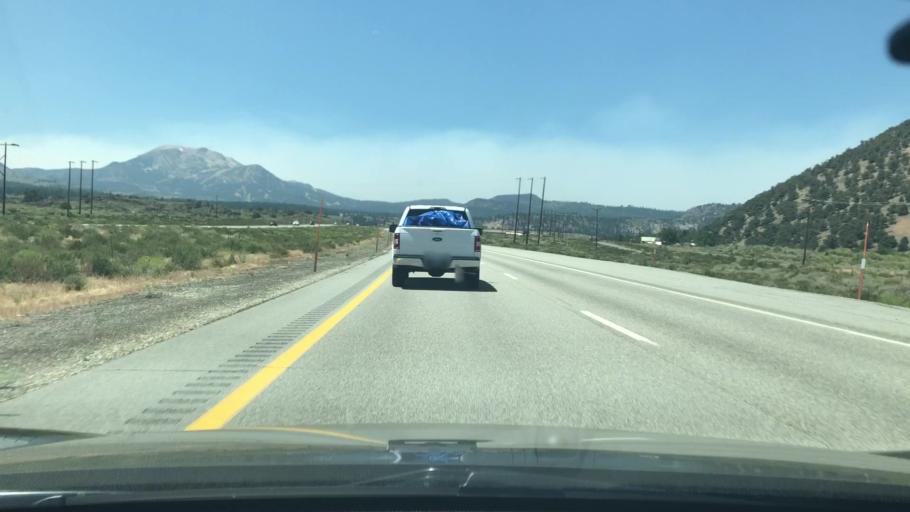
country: US
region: California
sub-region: Mono County
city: Mammoth Lakes
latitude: 37.6363
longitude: -118.8888
